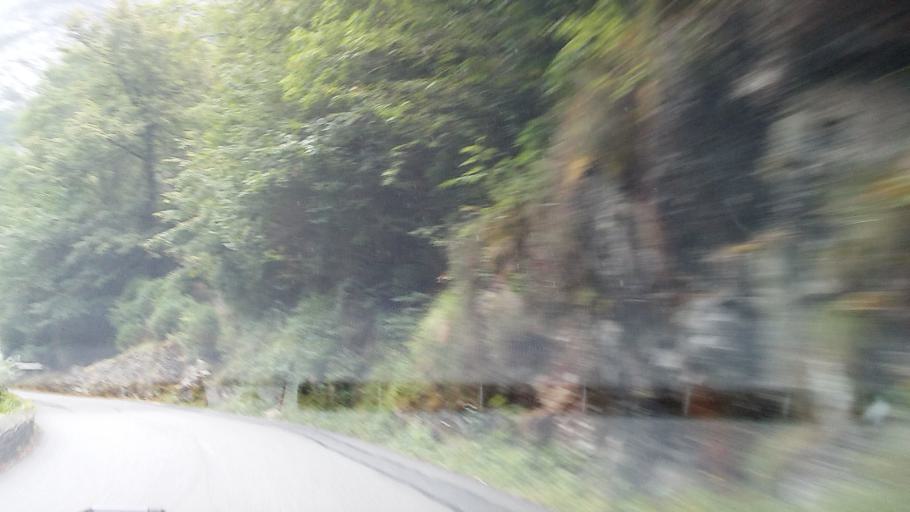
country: FR
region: Aquitaine
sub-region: Departement des Pyrenees-Atlantiques
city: Laruns
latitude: 42.9505
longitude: -0.4415
